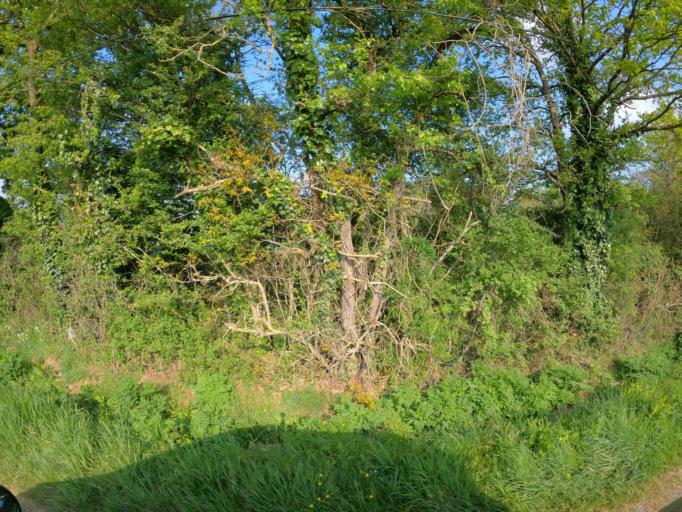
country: FR
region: Pays de la Loire
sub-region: Departement de Maine-et-Loire
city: Torfou
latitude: 47.0535
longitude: -1.0944
